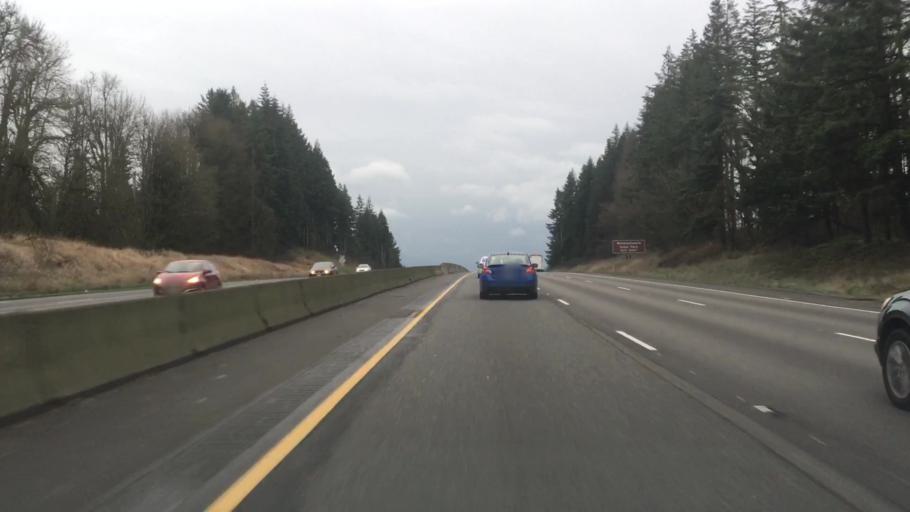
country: US
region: Washington
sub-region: Thurston County
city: Tumwater
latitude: 46.9036
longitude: -122.9576
